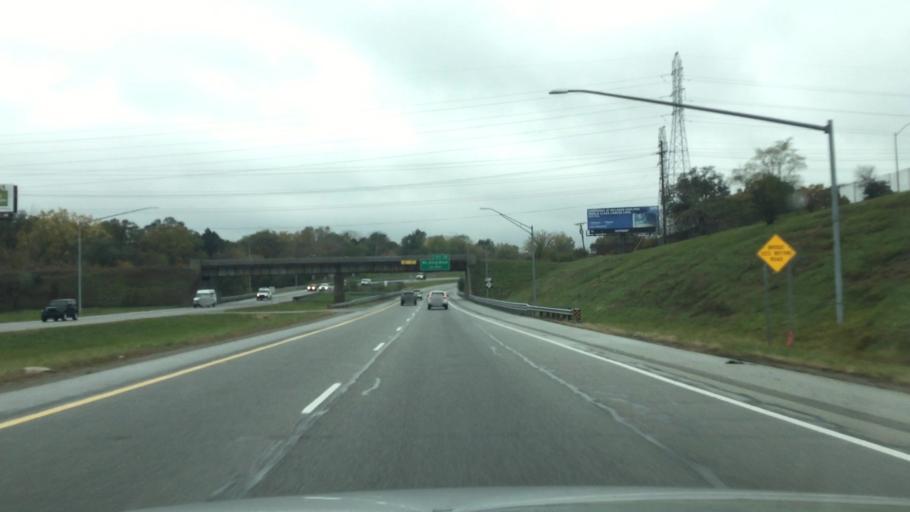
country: US
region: Michigan
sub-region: Oakland County
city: Pontiac
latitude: 42.6424
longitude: -83.2573
